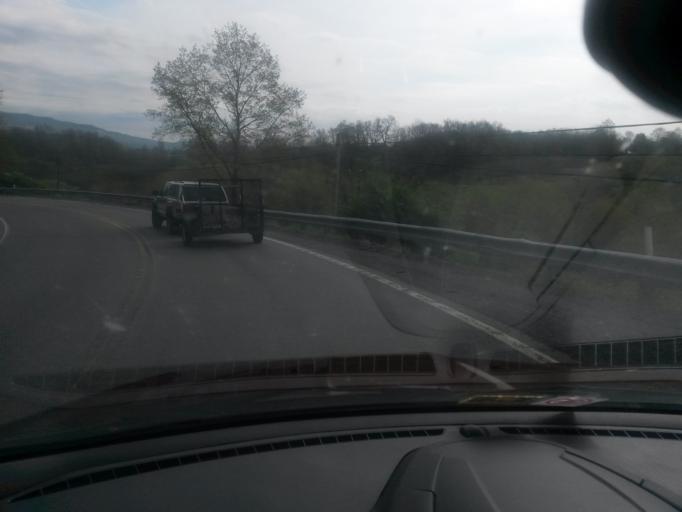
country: US
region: West Virginia
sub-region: Pocahontas County
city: Marlinton
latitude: 38.1196
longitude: -80.2411
